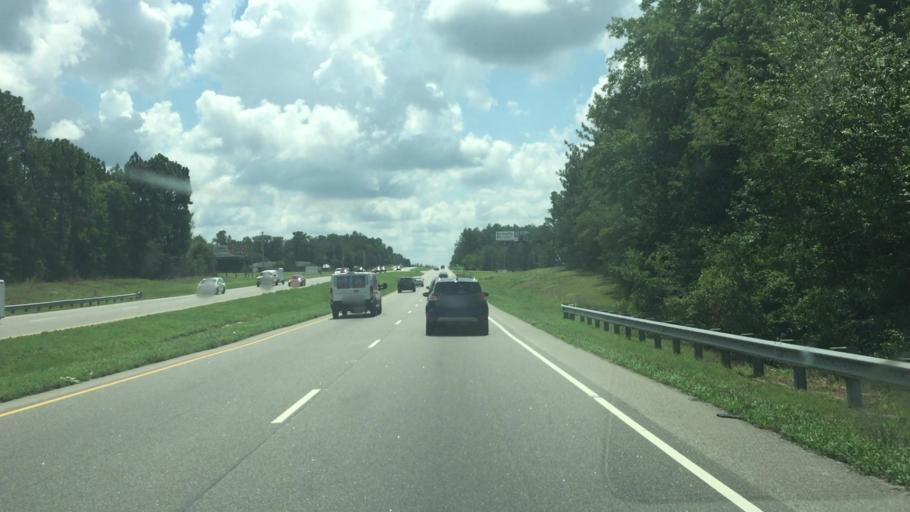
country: US
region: North Carolina
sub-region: Scotland County
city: Laurel Hill
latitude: 34.8464
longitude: -79.6117
